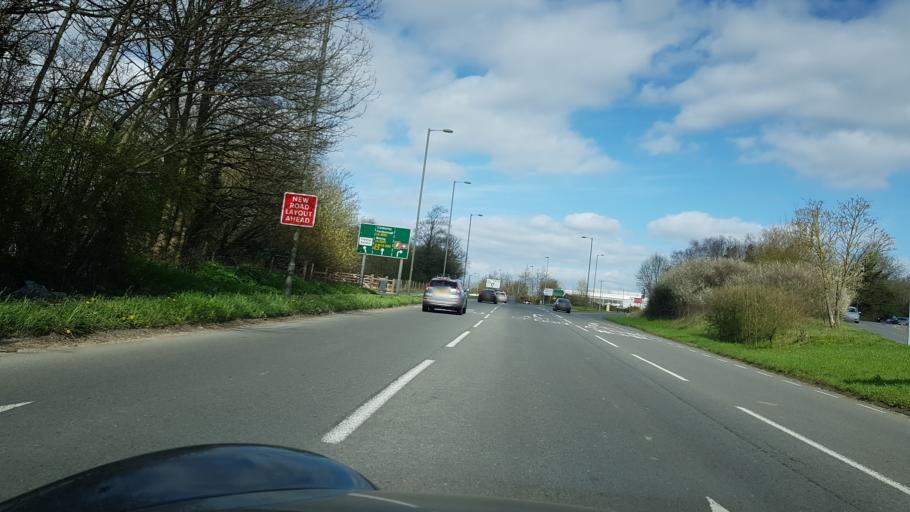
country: GB
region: England
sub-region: Surrey
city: Hale
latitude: 51.2199
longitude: -0.7798
